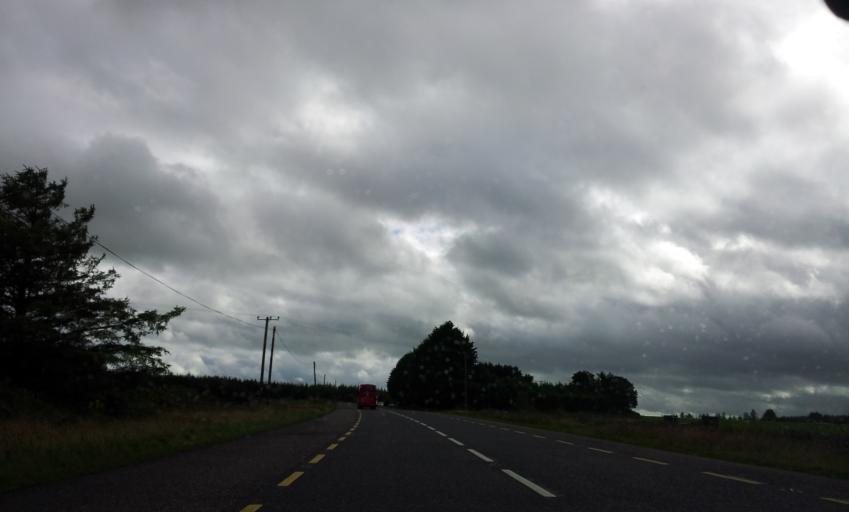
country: IE
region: Munster
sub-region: Waterford
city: Dungarvan
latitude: 52.0100
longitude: -7.7047
